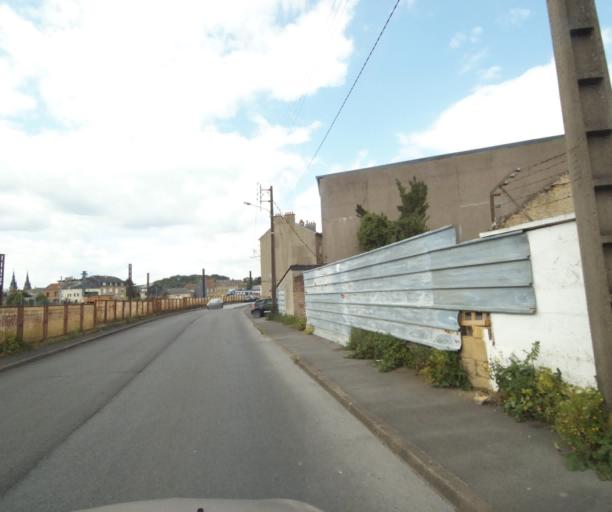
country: FR
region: Champagne-Ardenne
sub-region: Departement des Ardennes
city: Charleville-Mezieres
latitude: 49.7691
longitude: 4.7281
